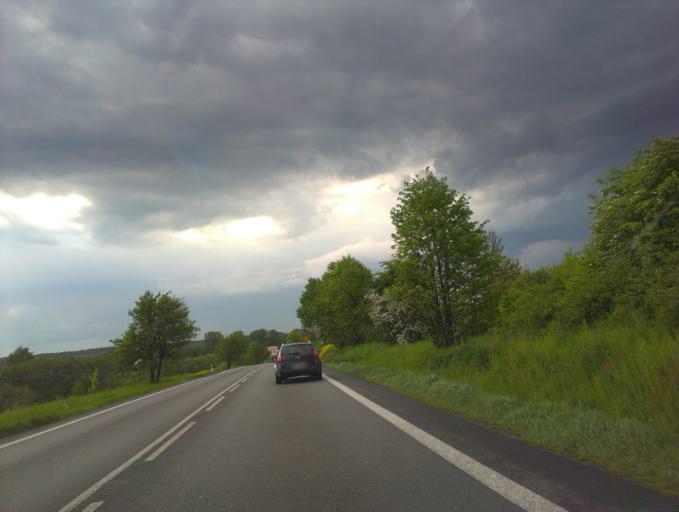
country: PL
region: Masovian Voivodeship
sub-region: Powiat grojecki
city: Pniewy
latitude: 51.8926
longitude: 20.7896
